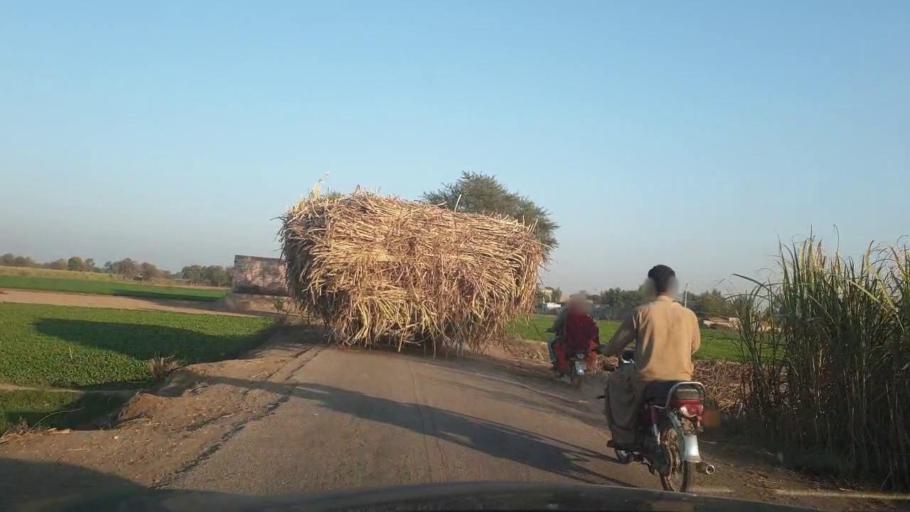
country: PK
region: Sindh
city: Ubauro
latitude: 28.1711
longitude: 69.5921
